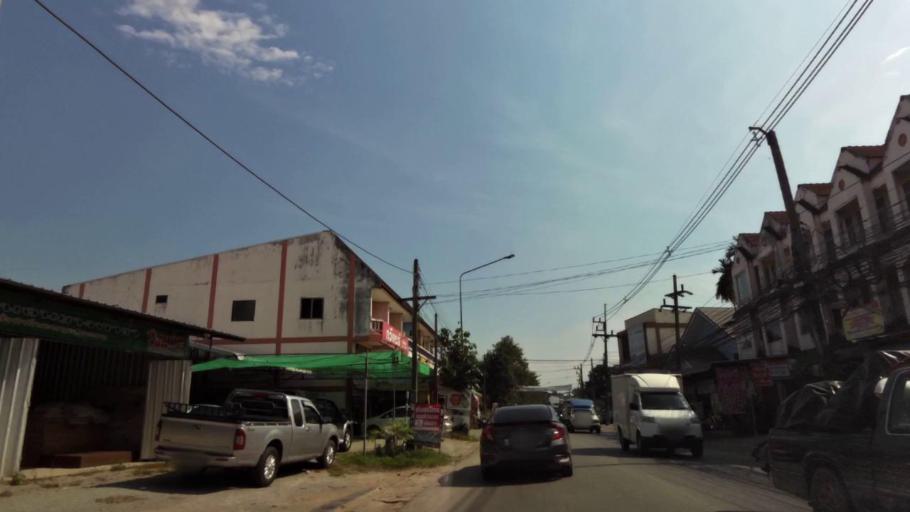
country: TH
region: Chiang Rai
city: Chiang Rai
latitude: 19.9260
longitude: 99.8369
